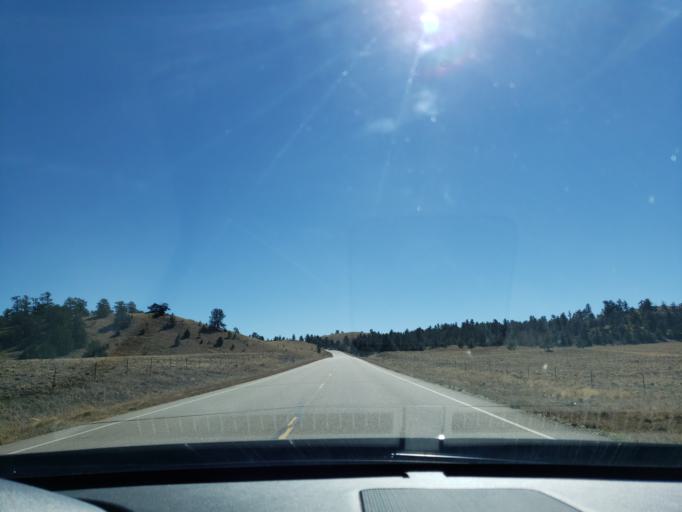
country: US
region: Colorado
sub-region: Chaffee County
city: Buena Vista
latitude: 38.8978
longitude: -105.6924
